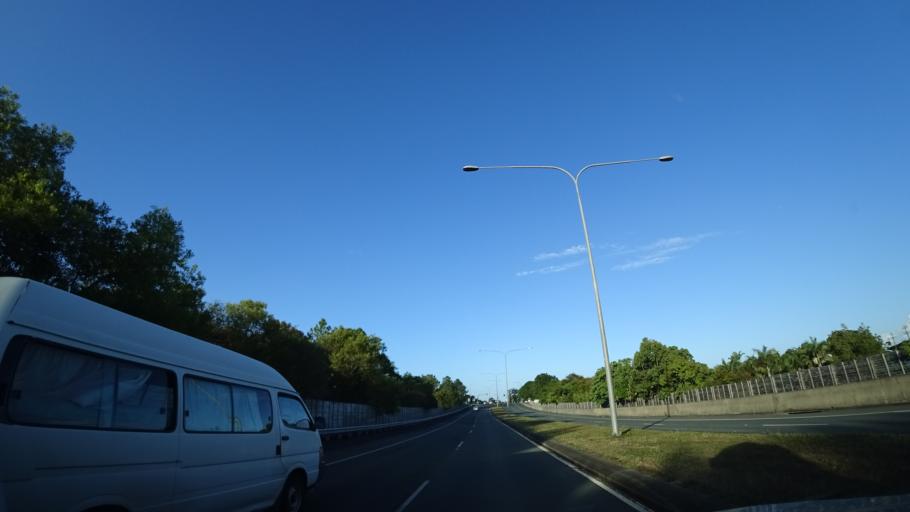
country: AU
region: Queensland
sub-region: Sunshine Coast
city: Buderim
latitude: -26.6578
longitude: 153.0699
